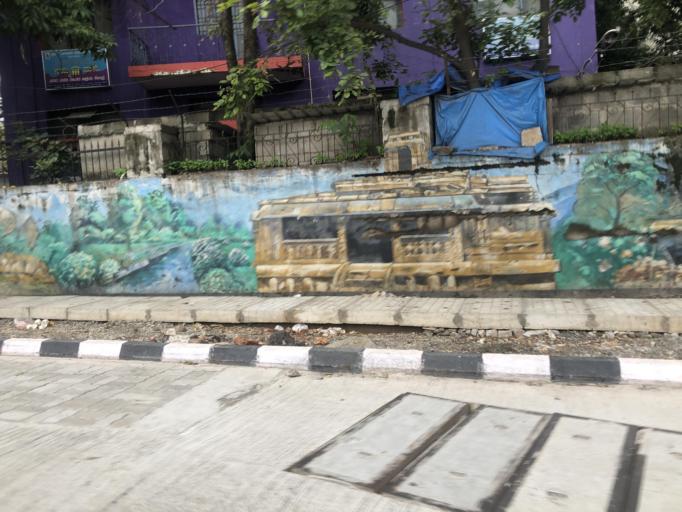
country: IN
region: Karnataka
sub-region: Bangalore Urban
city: Bangalore
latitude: 12.9743
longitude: 77.5696
